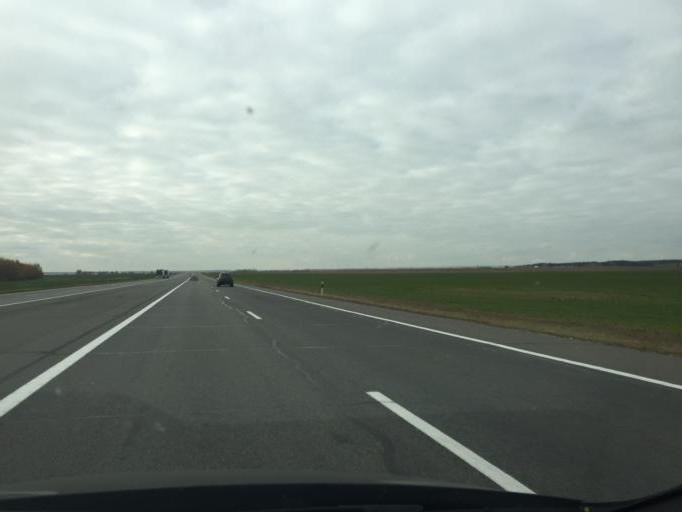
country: BY
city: Fanipol
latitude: 53.6843
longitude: 27.3088
